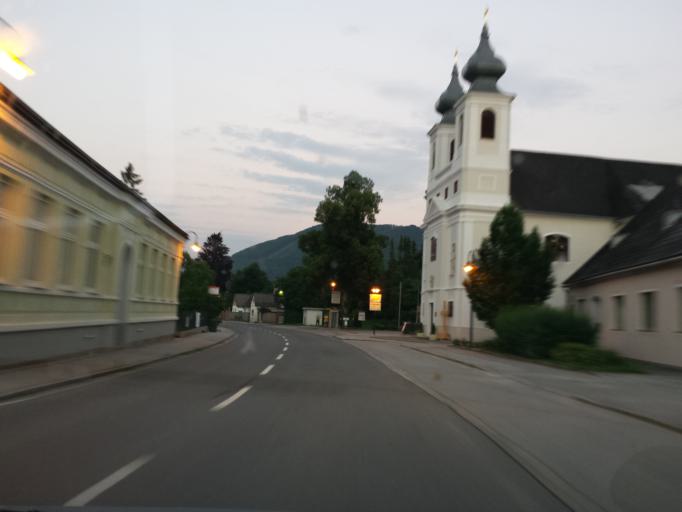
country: AT
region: Lower Austria
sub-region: Politischer Bezirk Baden
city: Altenmarkt an der Triesting
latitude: 48.0181
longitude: 15.9669
